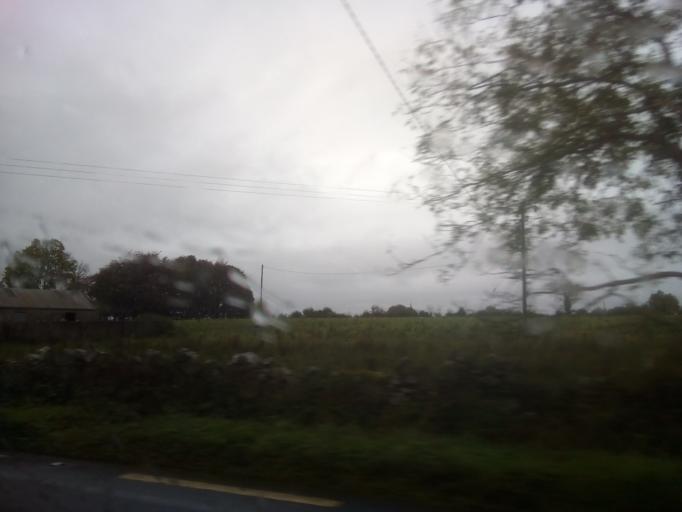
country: IE
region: Connaught
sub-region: Roscommon
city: Castlerea
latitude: 53.8336
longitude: -8.3746
